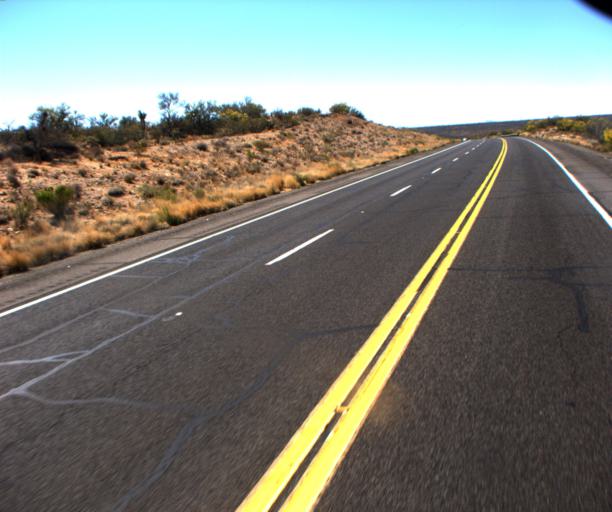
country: US
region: Arizona
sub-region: Yavapai County
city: Congress
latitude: 34.2246
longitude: -113.0694
